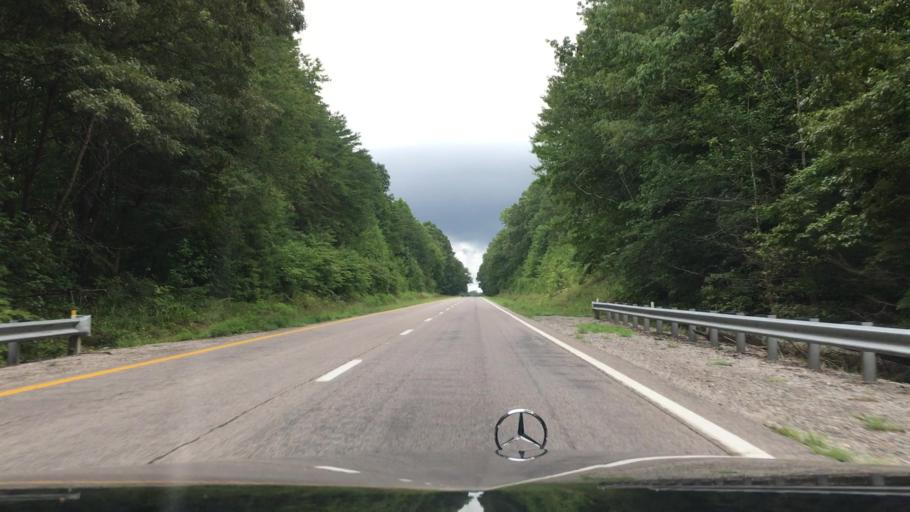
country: US
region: Virginia
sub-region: Appomattox County
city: Appomattox
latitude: 37.2699
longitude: -78.6689
